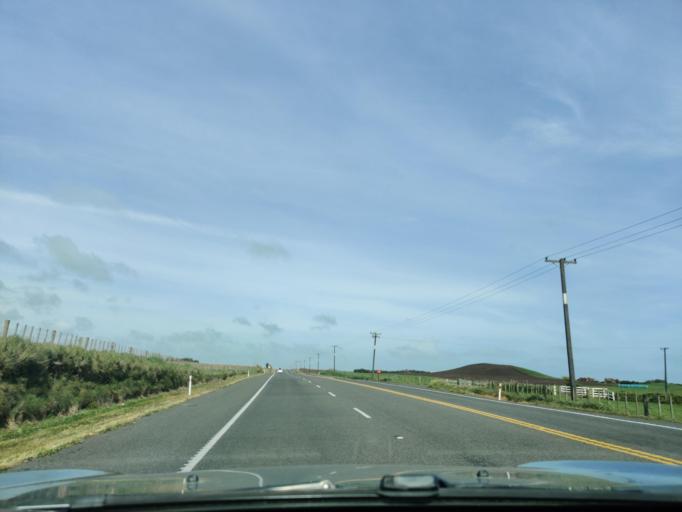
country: NZ
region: Taranaki
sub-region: South Taranaki District
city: Patea
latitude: -39.6904
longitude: 174.4230
